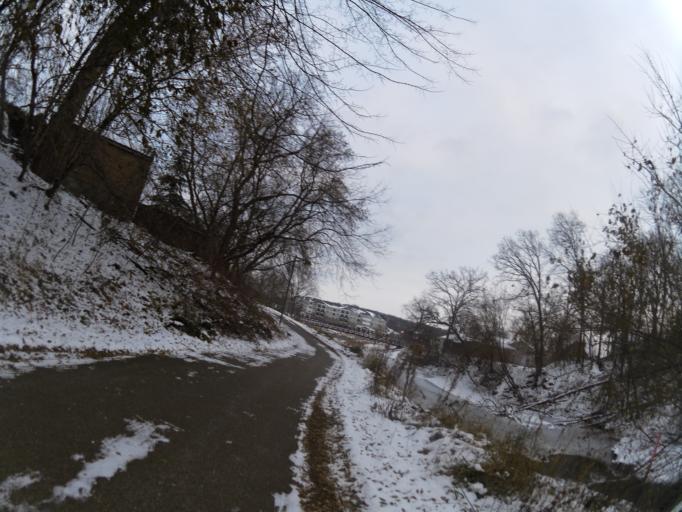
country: US
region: Minnesota
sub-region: Olmsted County
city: Rochester
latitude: 44.0369
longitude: -92.4670
